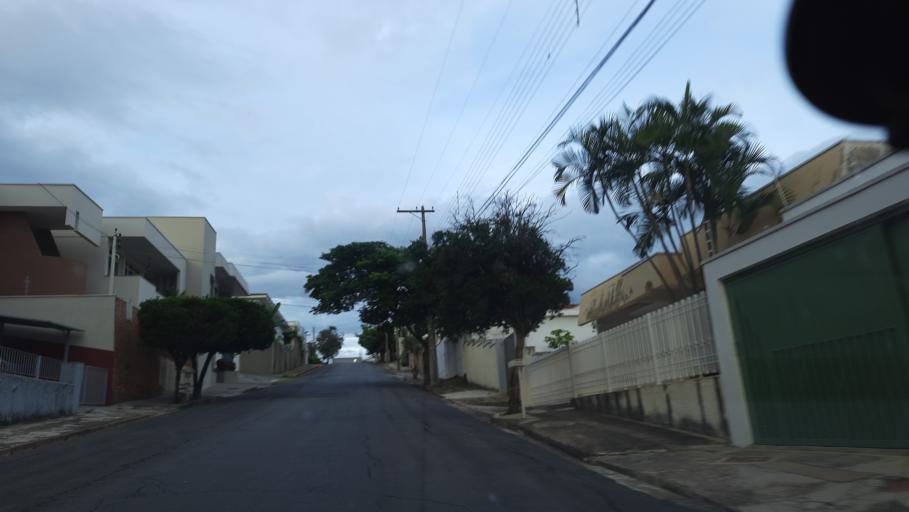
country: BR
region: Sao Paulo
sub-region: Sao Joao Da Boa Vista
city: Sao Joao da Boa Vista
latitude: -21.9664
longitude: -46.7927
